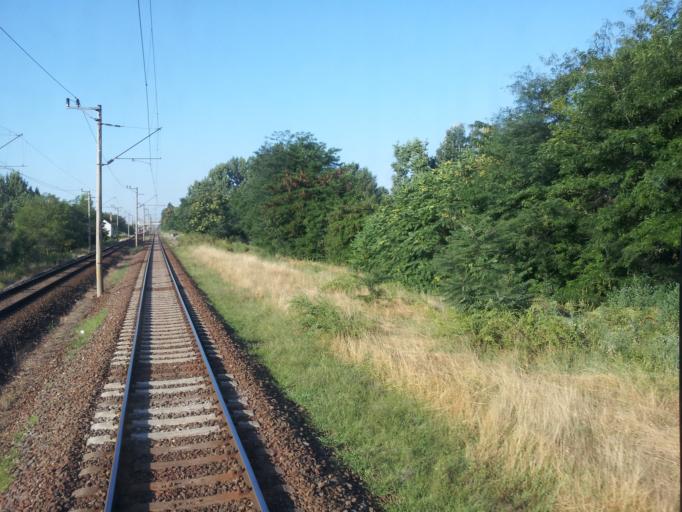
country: HU
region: Budapest
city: Budapest XXIII. keruelet
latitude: 47.3918
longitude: 19.1267
